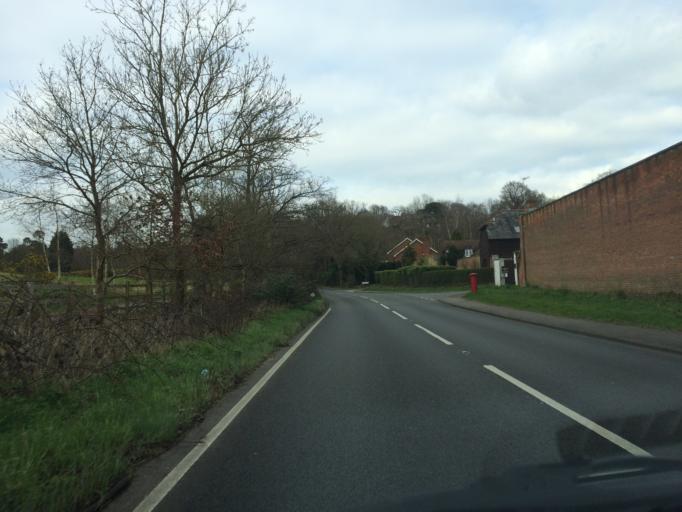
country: GB
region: England
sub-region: Surrey
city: Ottershaw
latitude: 51.3585
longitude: -0.5507
